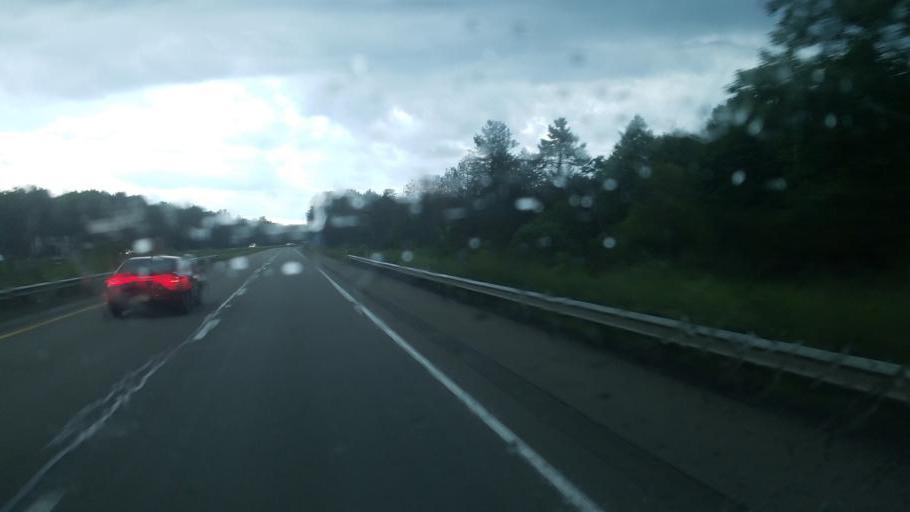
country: US
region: Pennsylvania
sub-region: Mercer County
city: Grove City
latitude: 41.1209
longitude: -80.1490
